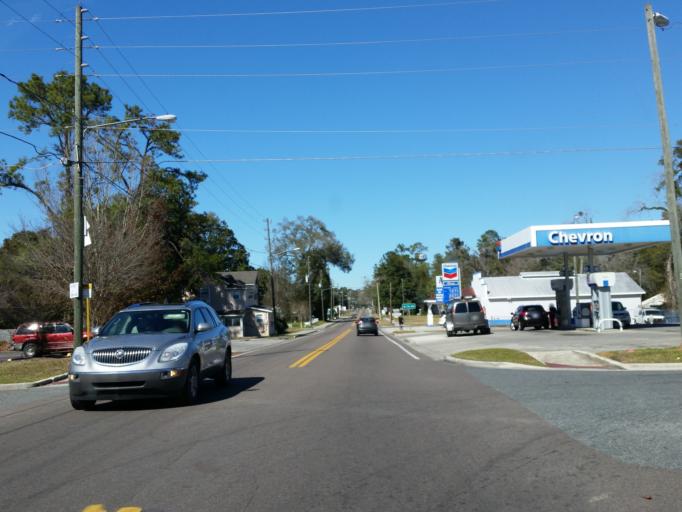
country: US
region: Florida
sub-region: Alachua County
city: Archer
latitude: 29.5300
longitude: -82.5191
